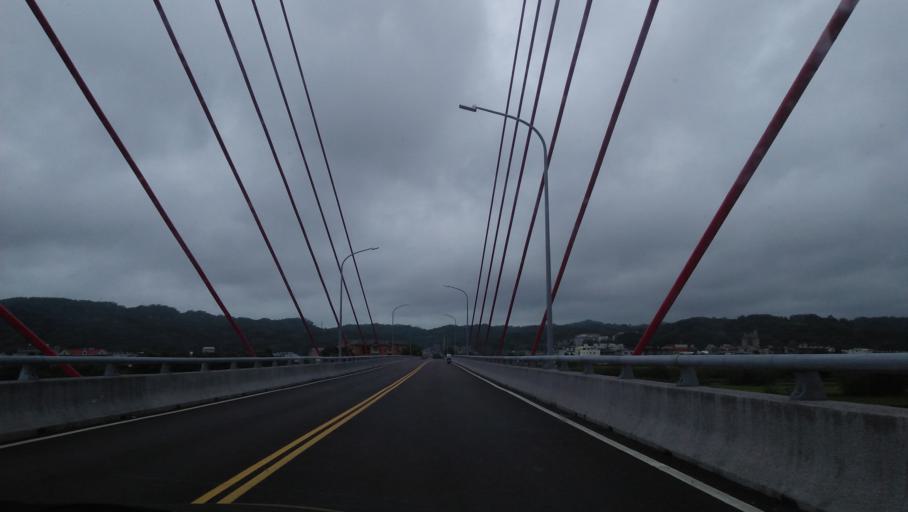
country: TW
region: Taiwan
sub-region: Hsinchu
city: Zhubei
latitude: 24.7863
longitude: 121.0584
